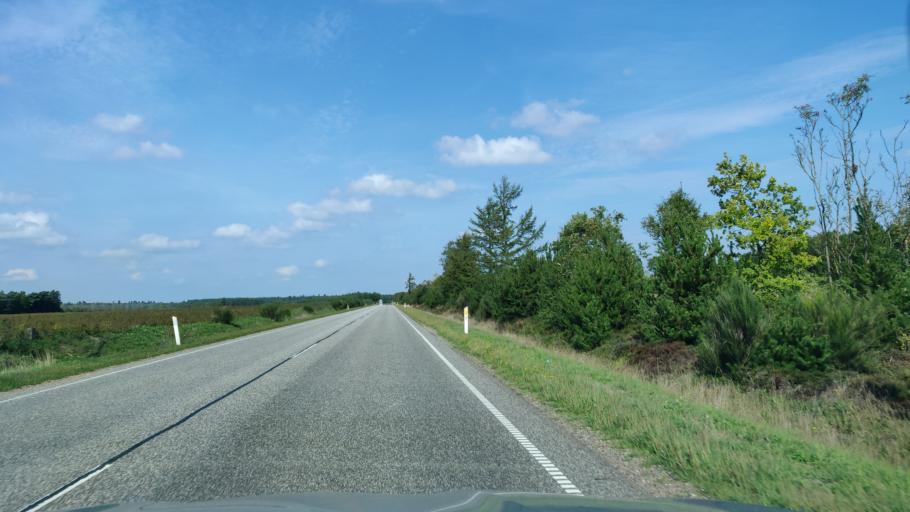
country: DK
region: Central Jutland
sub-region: Herning Kommune
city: Sunds
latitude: 56.3432
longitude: 8.9783
